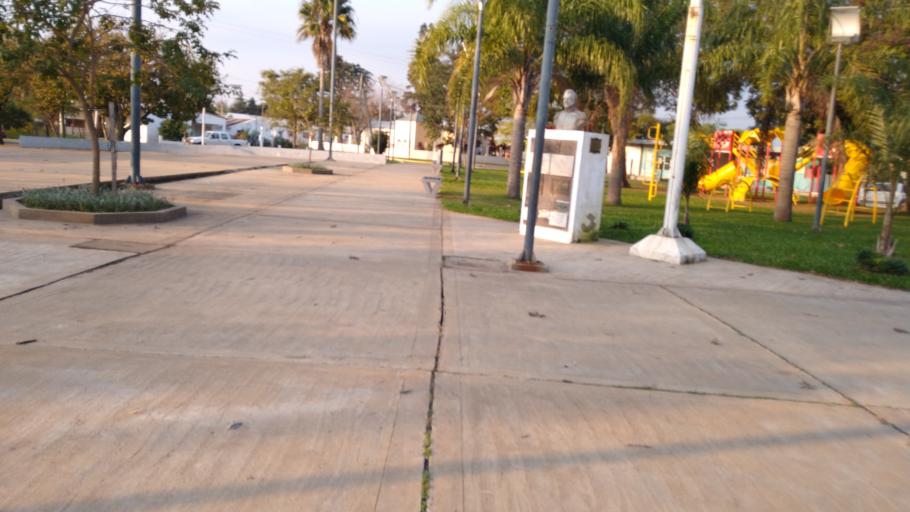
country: AR
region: Entre Rios
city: Santa Ana
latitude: -30.8995
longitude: -57.9313
